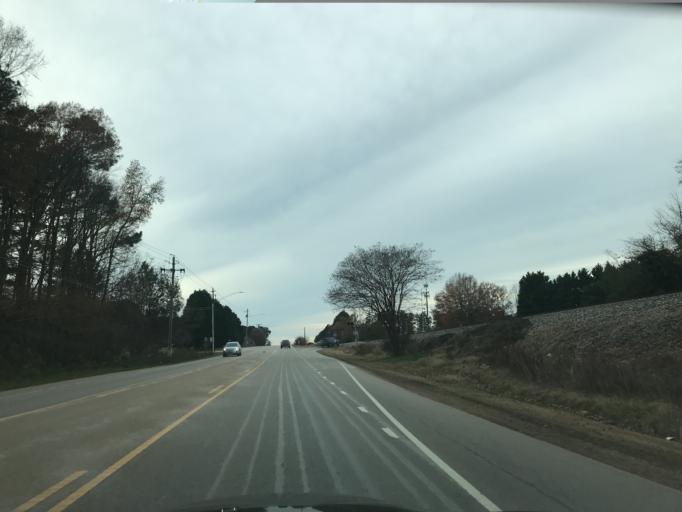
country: US
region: North Carolina
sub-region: Wake County
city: Cary
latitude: 35.7897
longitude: -78.7490
